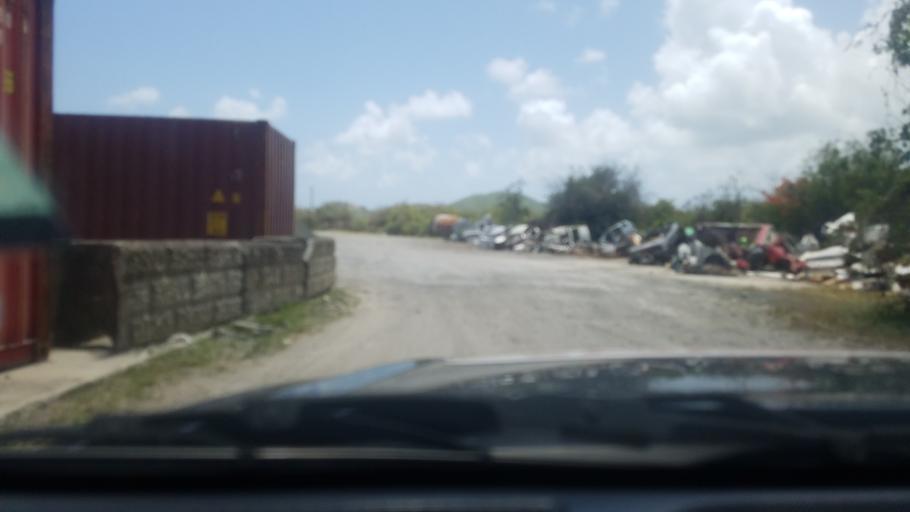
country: LC
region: Vieux-Fort
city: Vieux Fort
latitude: 13.7462
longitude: -60.9453
